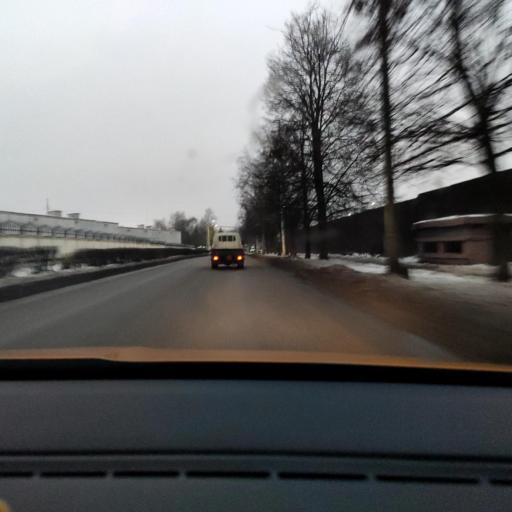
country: RU
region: Moskovskaya
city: Mosrentgen
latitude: 55.6158
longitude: 37.4656
